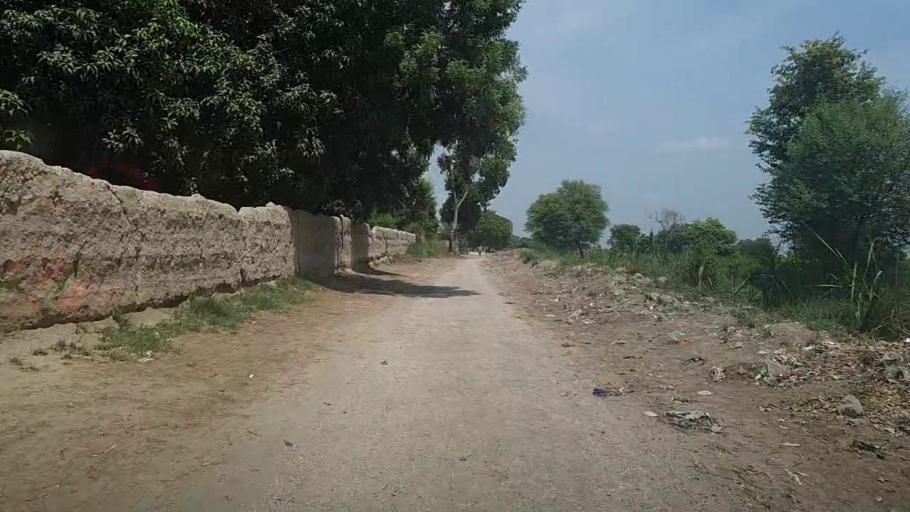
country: PK
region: Sindh
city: Ubauro
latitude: 28.2958
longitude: 69.8013
